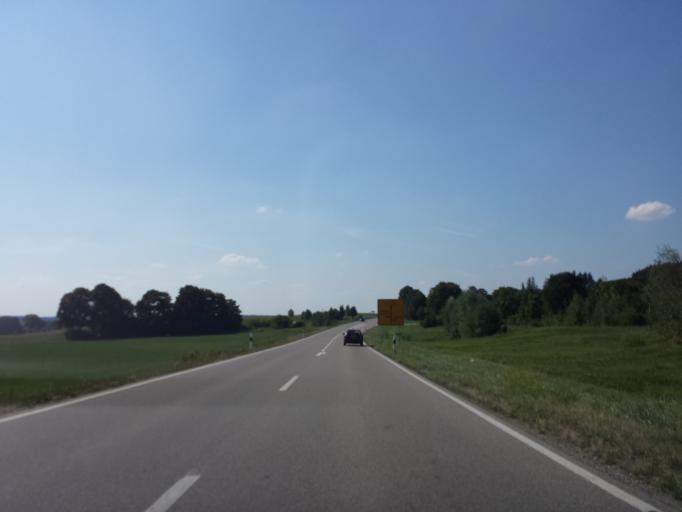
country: DE
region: Bavaria
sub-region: Swabia
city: Breitenbrunn
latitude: 48.1379
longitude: 10.4270
